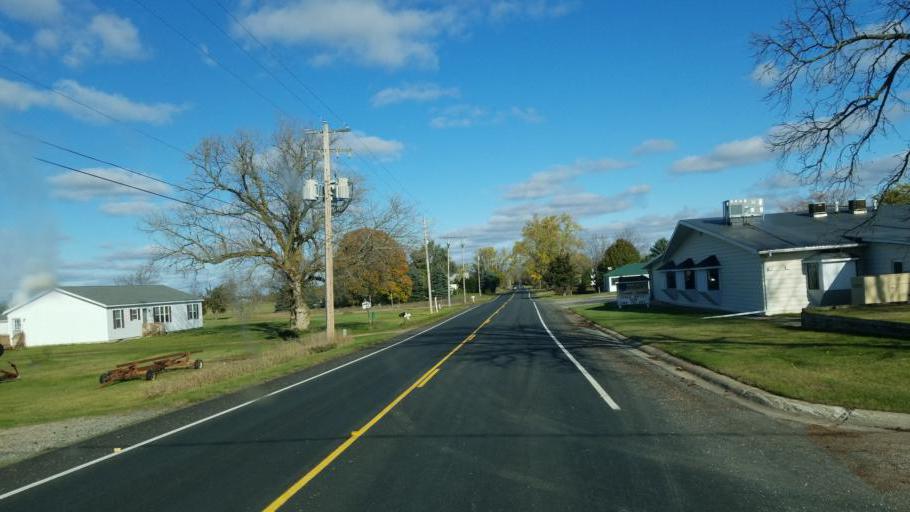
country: US
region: Michigan
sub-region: Montcalm County
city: Edmore
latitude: 43.4546
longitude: -85.0443
